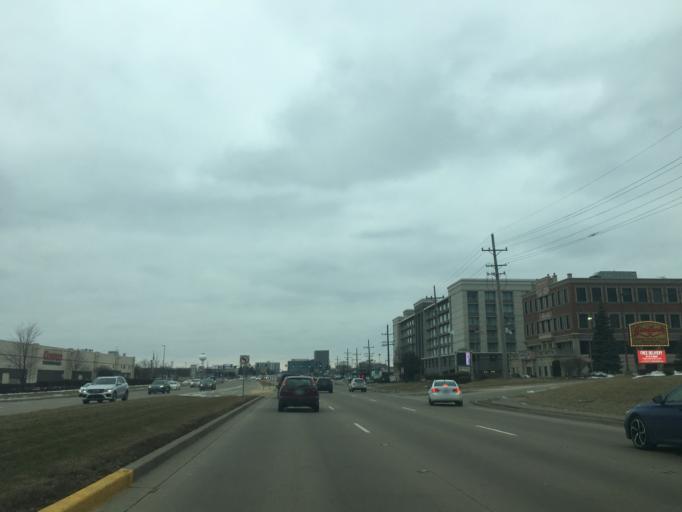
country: US
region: Illinois
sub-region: DuPage County
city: Oakbrook Terrace
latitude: 41.8465
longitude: -87.9647
